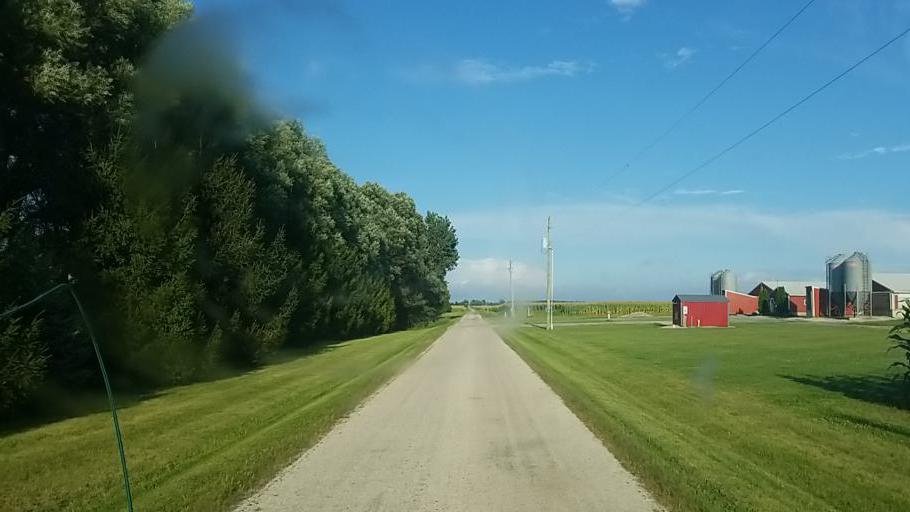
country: US
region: Ohio
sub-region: Crawford County
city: Bucyrus
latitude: 40.7394
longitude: -82.9872
